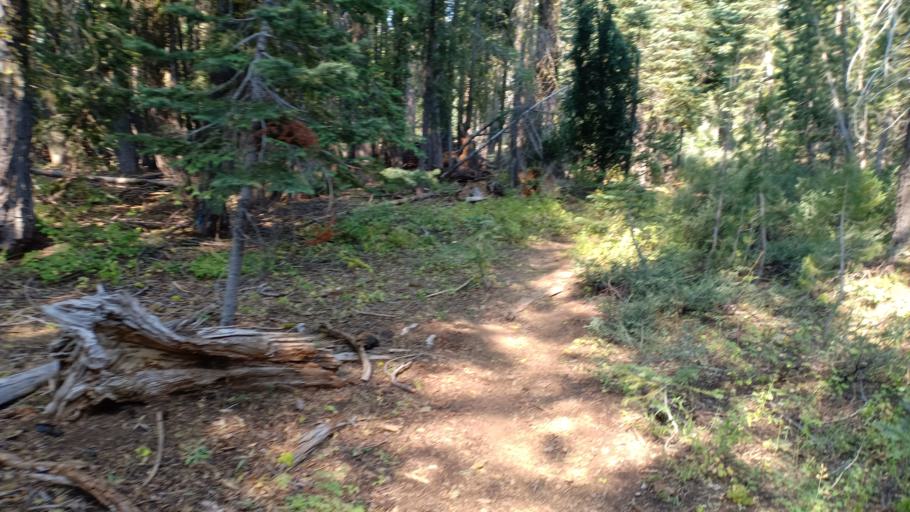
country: US
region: California
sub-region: Placer County
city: Sunnyside-Tahoe City
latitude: 39.1485
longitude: -120.1752
